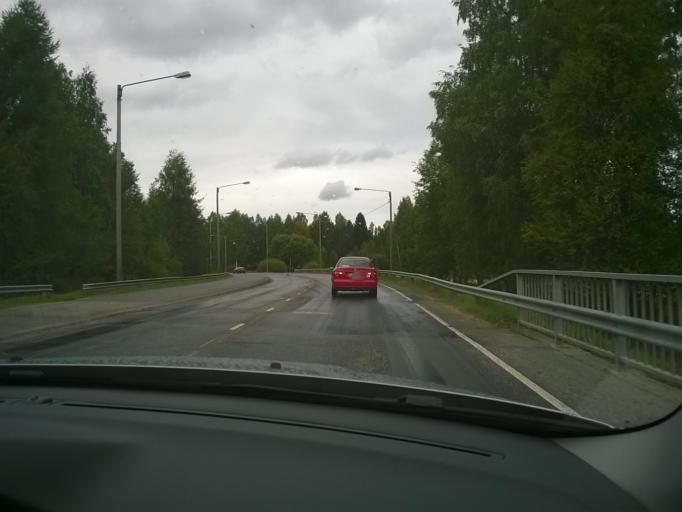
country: FI
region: Kainuu
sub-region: Kehys-Kainuu
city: Kuhmo
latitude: 64.1277
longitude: 29.5021
